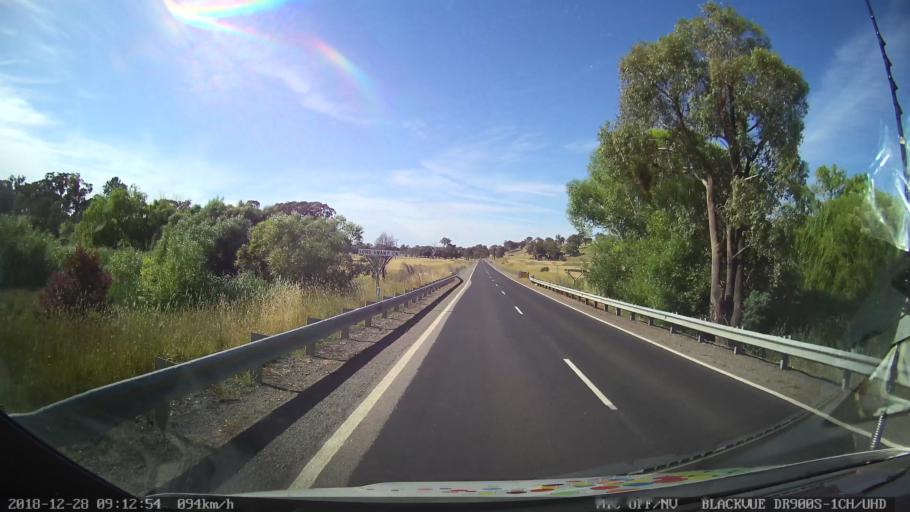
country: AU
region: New South Wales
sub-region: Upper Lachlan Shire
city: Crookwell
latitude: -34.2618
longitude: 149.3429
